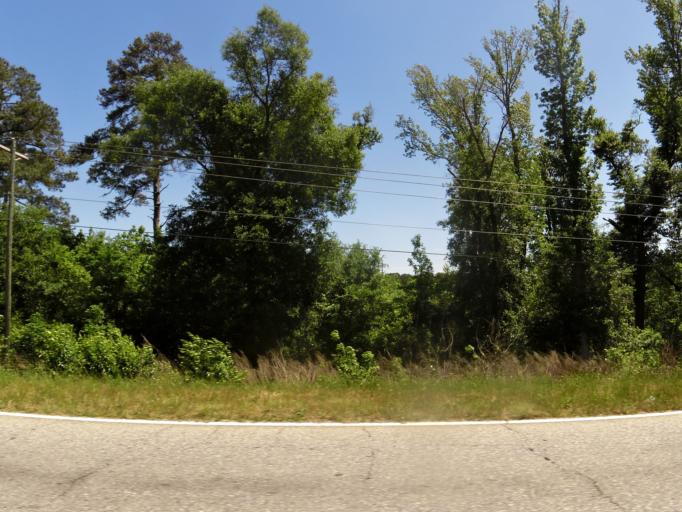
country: US
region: South Carolina
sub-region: Aiken County
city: Burnettown
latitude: 33.5136
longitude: -81.8646
